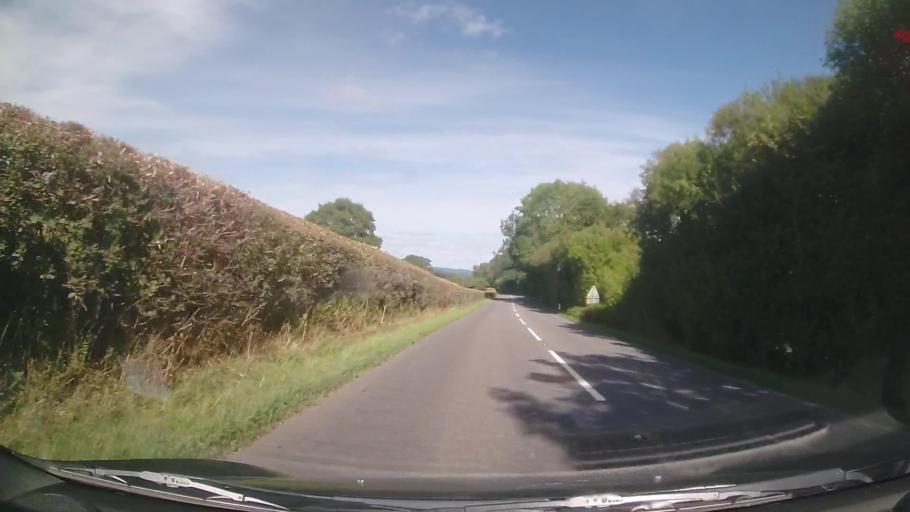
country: GB
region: England
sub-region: Herefordshire
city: Kington
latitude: 52.1793
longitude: -3.0308
